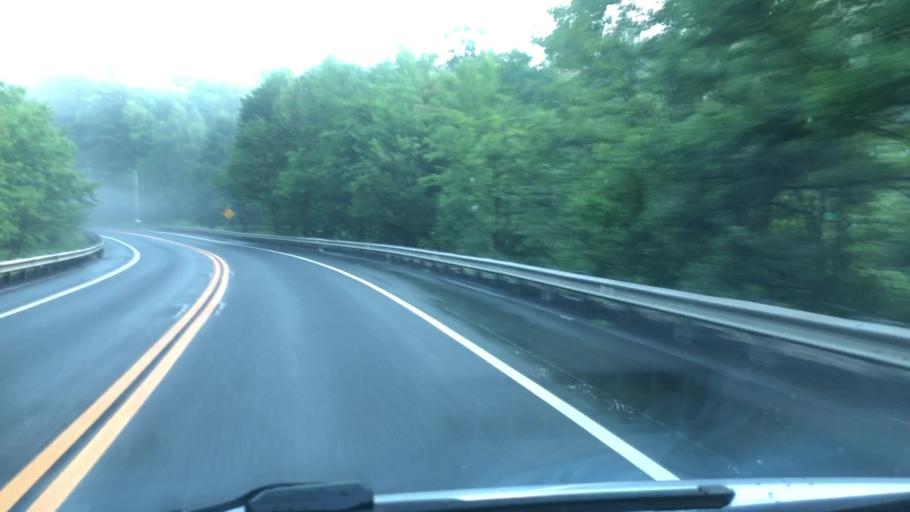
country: US
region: Massachusetts
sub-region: Hampshire County
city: Chesterfield
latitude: 42.4521
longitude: -72.8225
